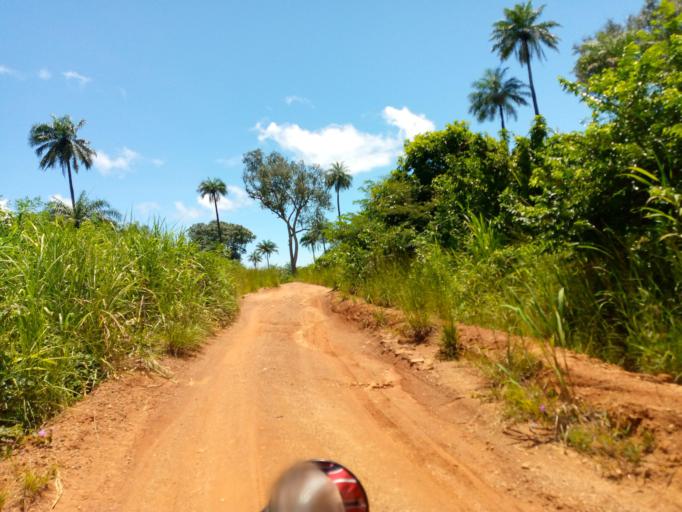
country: SL
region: Northern Province
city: Binkolo
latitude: 9.1167
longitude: -12.1755
